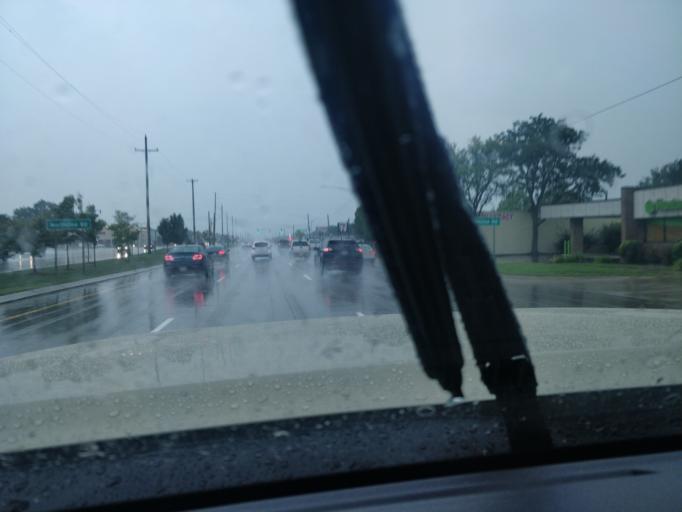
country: US
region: Michigan
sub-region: Wayne County
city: Southgate
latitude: 42.2152
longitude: -83.1811
